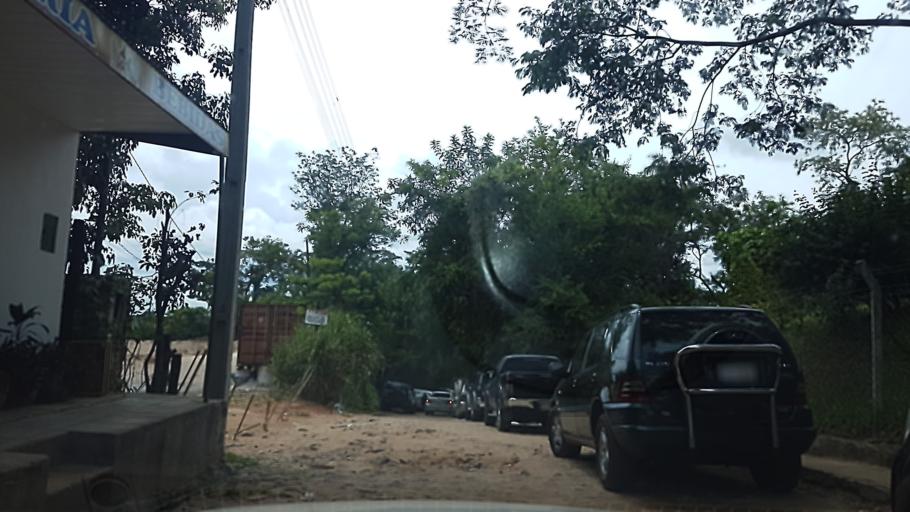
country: PY
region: Central
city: Colonia Mariano Roque Alonso
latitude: -25.1836
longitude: -57.5389
